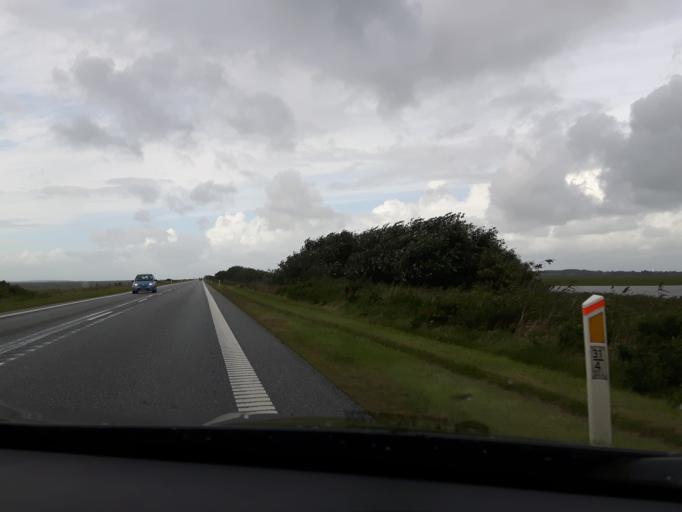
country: DK
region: North Denmark
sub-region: Jammerbugt Kommune
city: Fjerritslev
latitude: 57.0371
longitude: 9.1187
